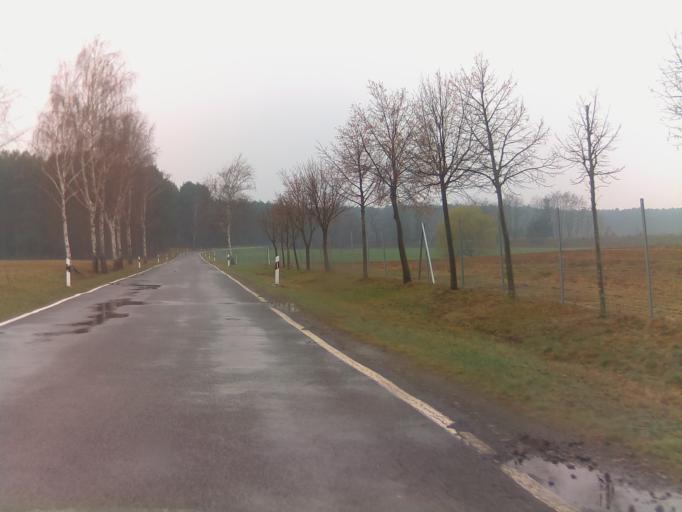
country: DE
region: Brandenburg
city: Jamlitz
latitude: 52.0358
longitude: 14.3654
